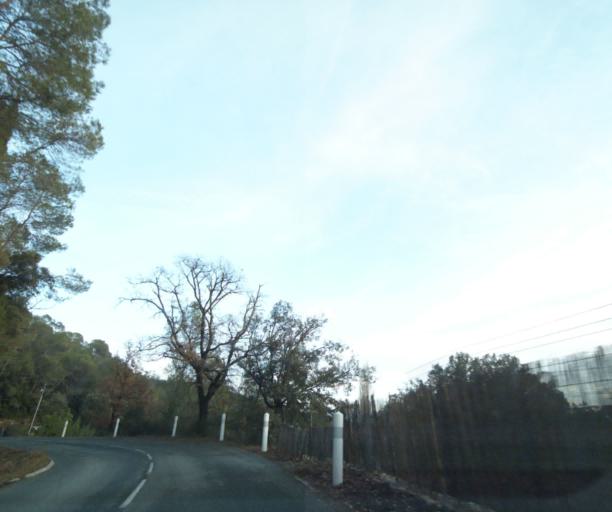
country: FR
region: Provence-Alpes-Cote d'Azur
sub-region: Departement du Var
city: Trans-en-Provence
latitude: 43.4974
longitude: 6.5033
